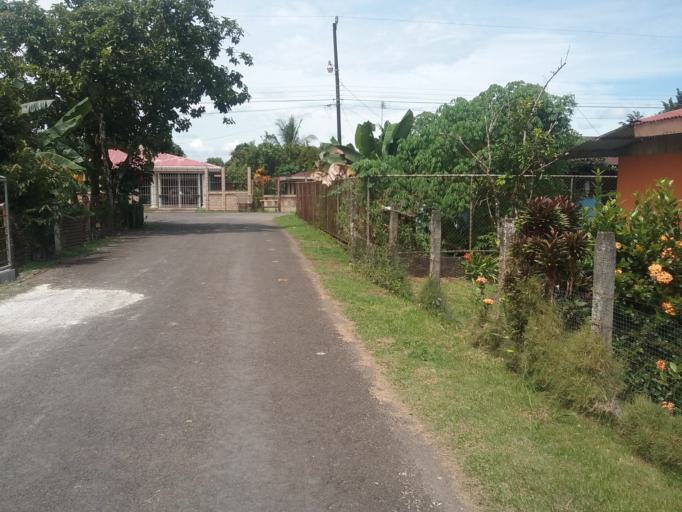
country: CR
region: Limon
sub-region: Canton de Pococi
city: Roxana
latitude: 10.3248
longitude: -83.8857
